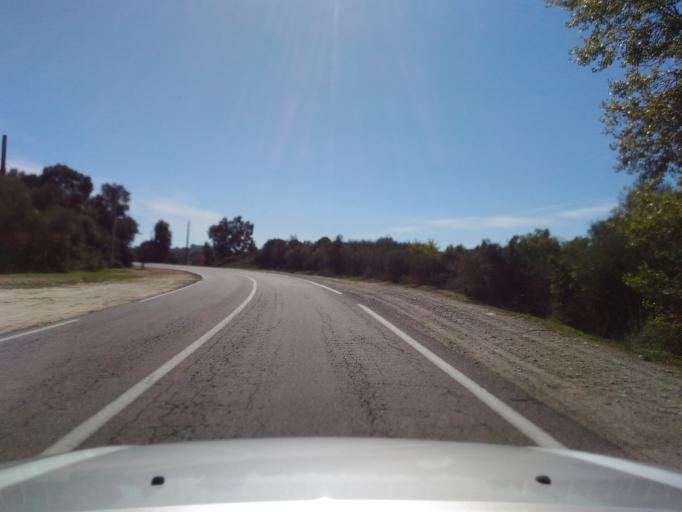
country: FR
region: Corsica
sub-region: Departement de la Haute-Corse
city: Aleria
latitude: 42.1165
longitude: 9.4915
